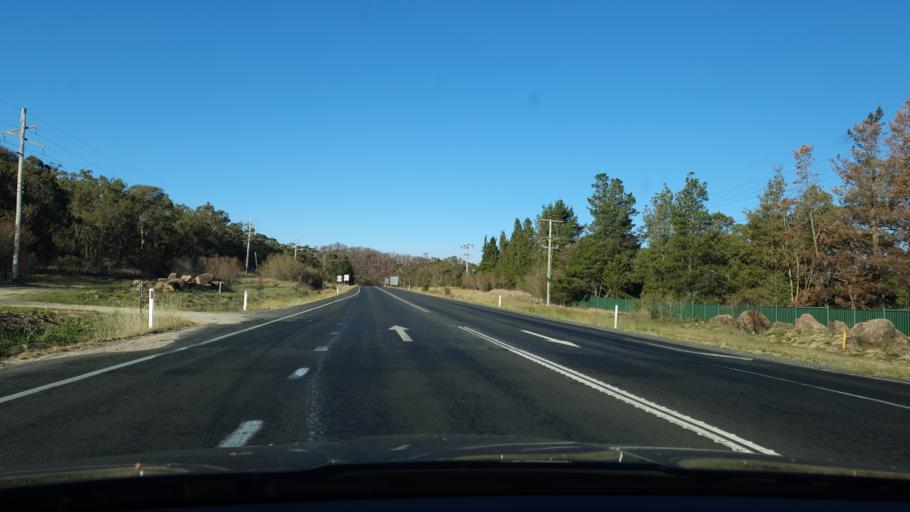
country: AU
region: Queensland
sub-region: Southern Downs
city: Stanthorpe
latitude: -28.6489
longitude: 151.9234
